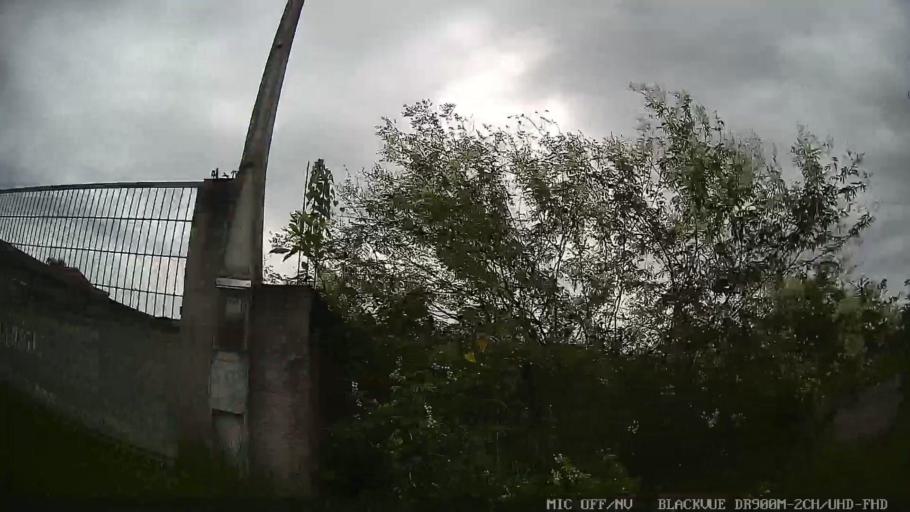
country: BR
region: Sao Paulo
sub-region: Caraguatatuba
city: Caraguatatuba
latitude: -23.6779
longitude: -45.4549
